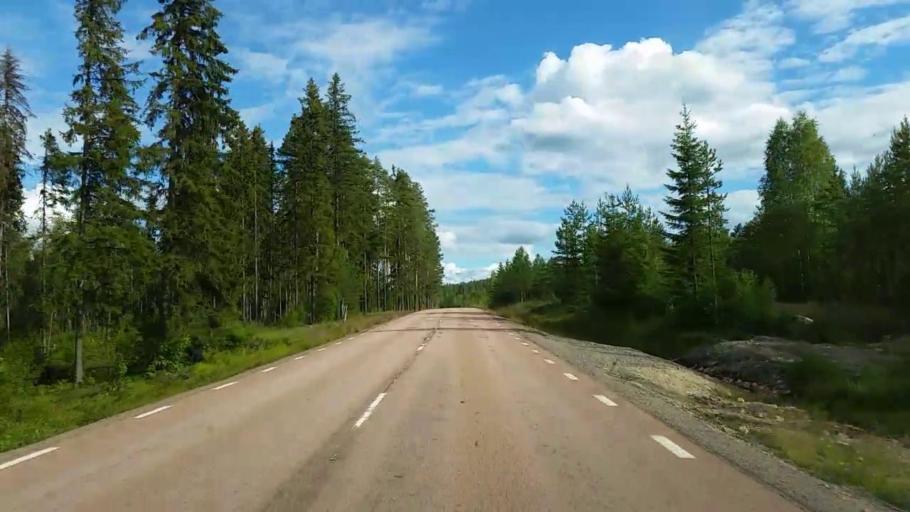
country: SE
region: Gaevleborg
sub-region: Ljusdals Kommun
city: Farila
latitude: 61.9762
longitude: 15.8601
